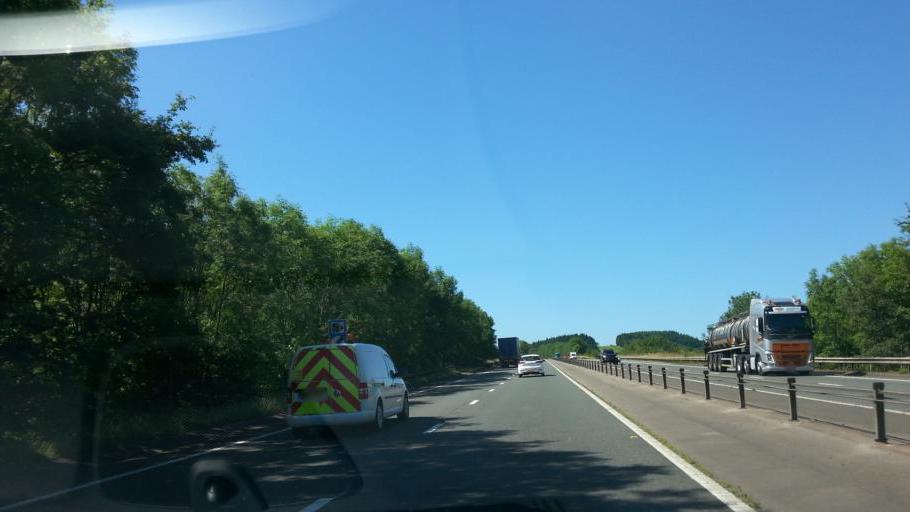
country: GB
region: Wales
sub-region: Newport
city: Langstone
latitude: 51.6272
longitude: -2.8989
